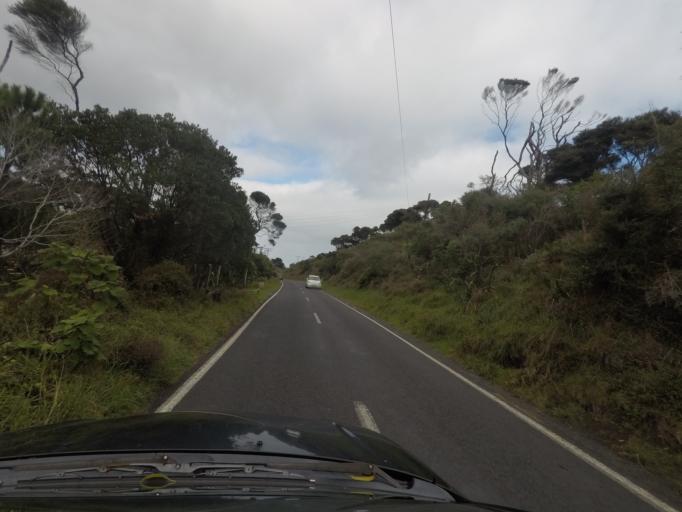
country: NZ
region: Auckland
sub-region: Auckland
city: Muriwai Beach
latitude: -36.8847
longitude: 174.4522
